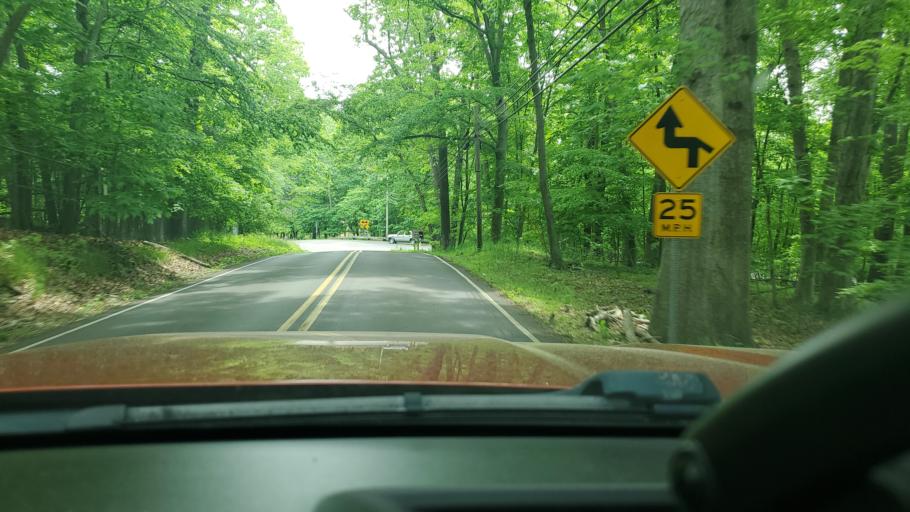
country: US
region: Pennsylvania
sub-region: Montgomery County
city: Red Hill
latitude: 40.3388
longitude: -75.4775
